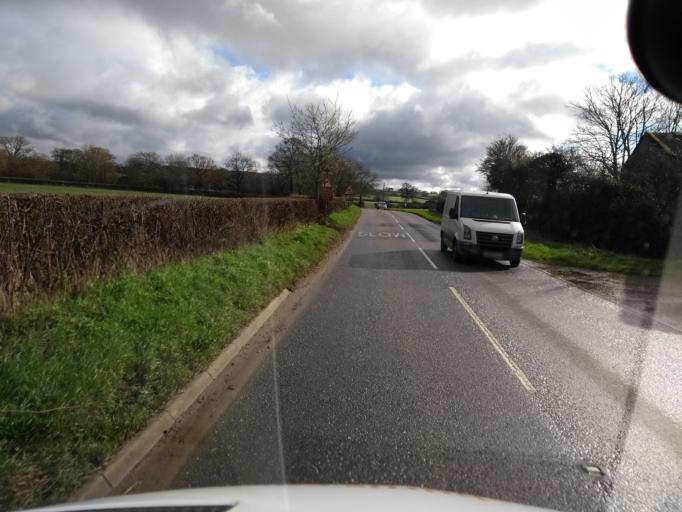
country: GB
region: England
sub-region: Somerset
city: Milborne Port
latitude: 50.9215
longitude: -2.4672
